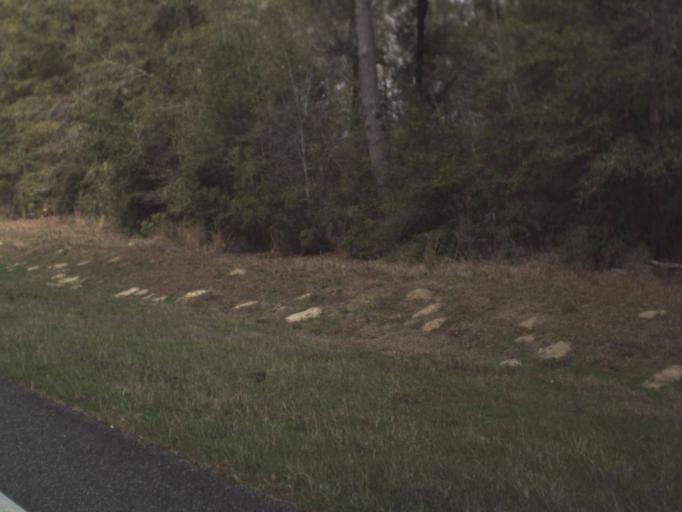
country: US
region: Florida
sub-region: Leon County
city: Woodville
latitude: 30.4134
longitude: -84.0823
